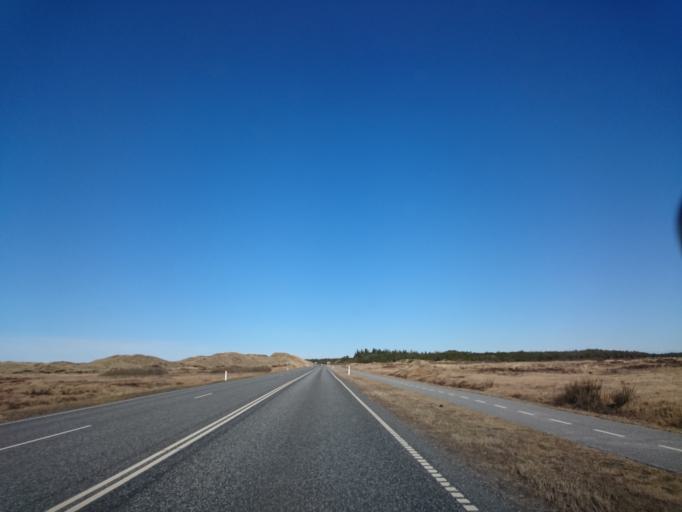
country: DK
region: North Denmark
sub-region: Frederikshavn Kommune
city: Skagen
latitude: 57.6919
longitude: 10.4729
